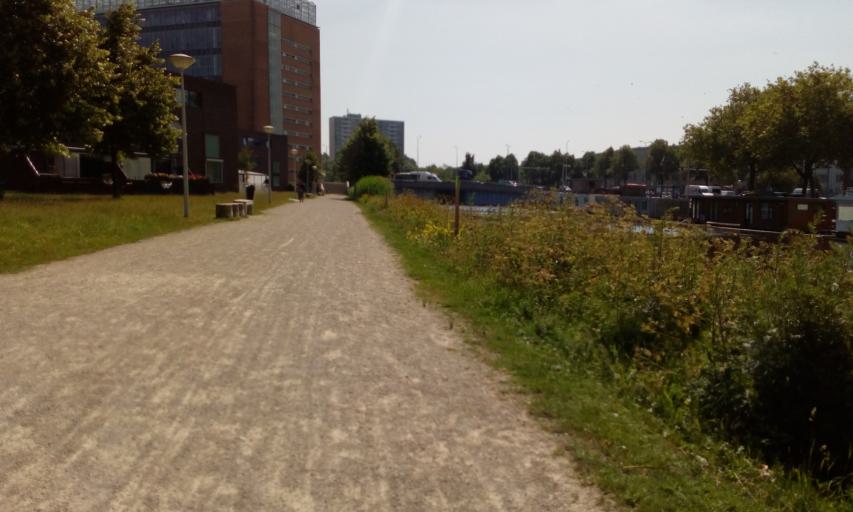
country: NL
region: South Holland
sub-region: Gemeente Den Haag
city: The Hague
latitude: 52.0577
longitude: 4.3005
